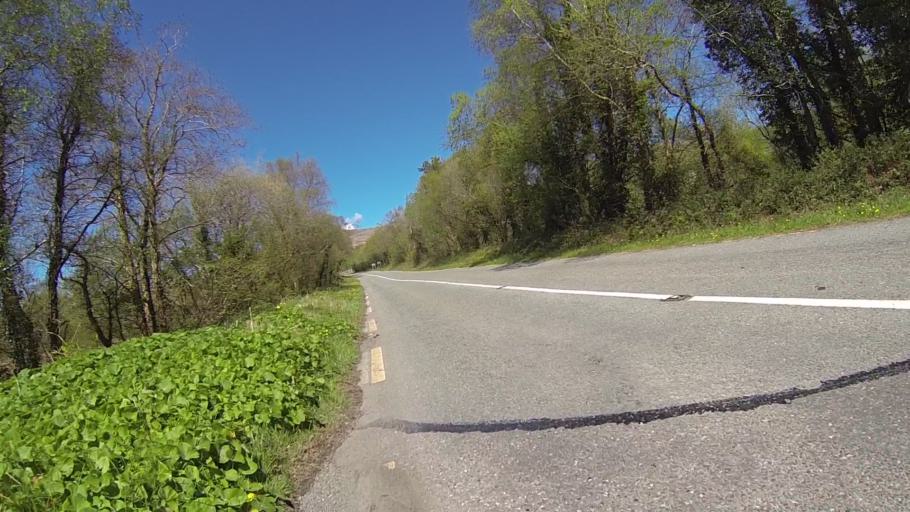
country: IE
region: Munster
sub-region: Ciarrai
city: Kenmare
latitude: 51.9023
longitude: -9.5987
